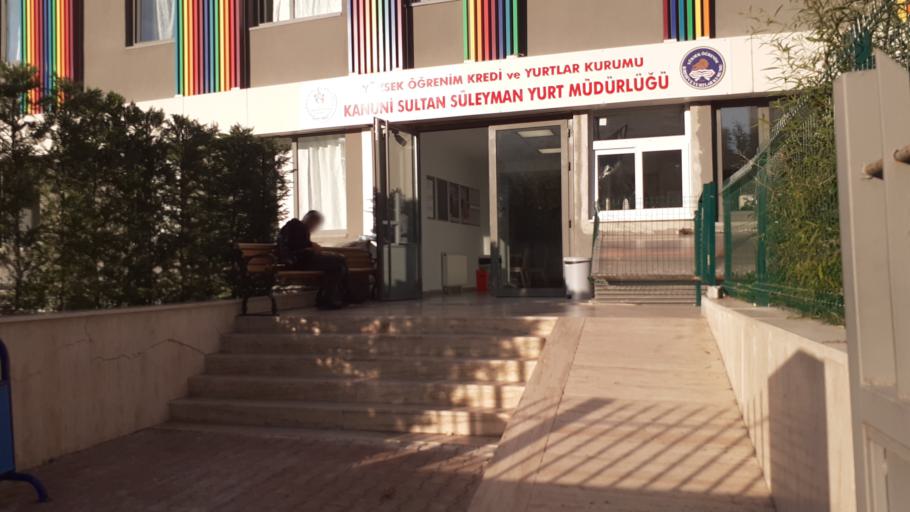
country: TR
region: Istanbul
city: Basaksehir
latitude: 41.0666
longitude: 28.7793
